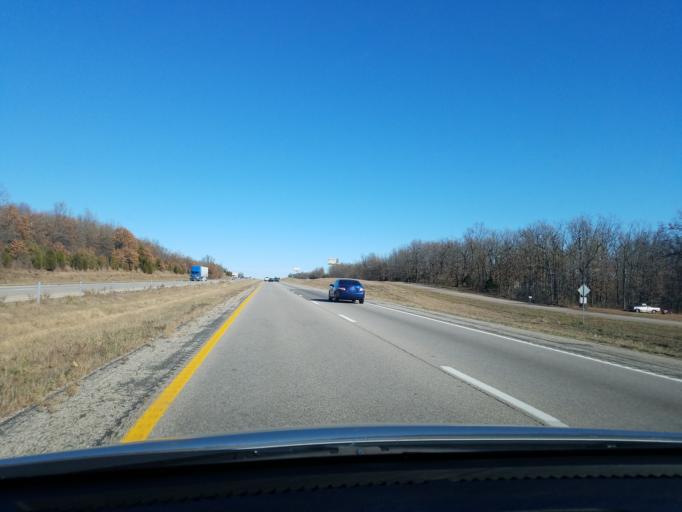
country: US
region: Missouri
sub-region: Laclede County
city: Lebanon
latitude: 37.5846
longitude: -92.7426
